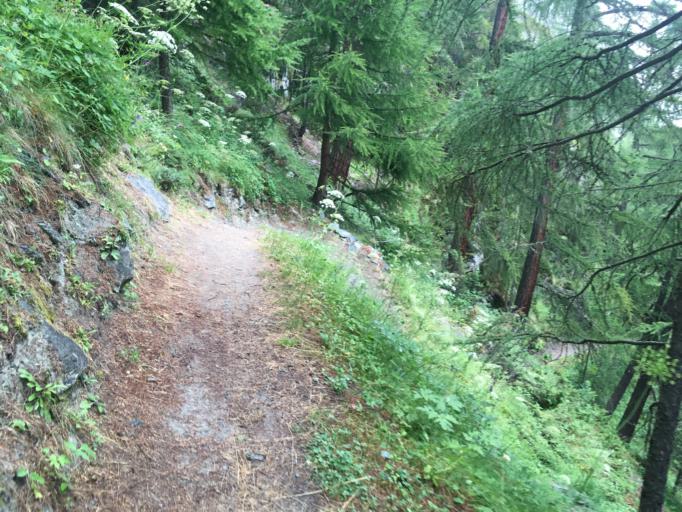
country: CH
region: Valais
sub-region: Visp District
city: Zermatt
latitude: 46.0084
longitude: 7.7275
